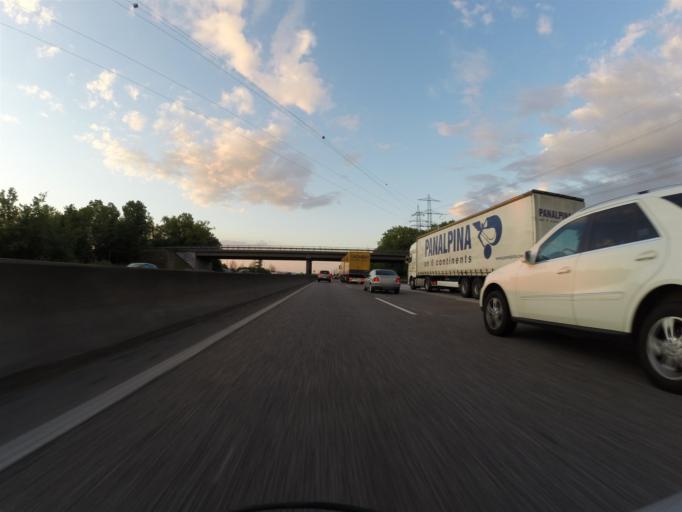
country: DE
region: Hesse
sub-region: Regierungsbezirk Darmstadt
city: Eschborn
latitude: 50.1520
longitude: 8.6005
